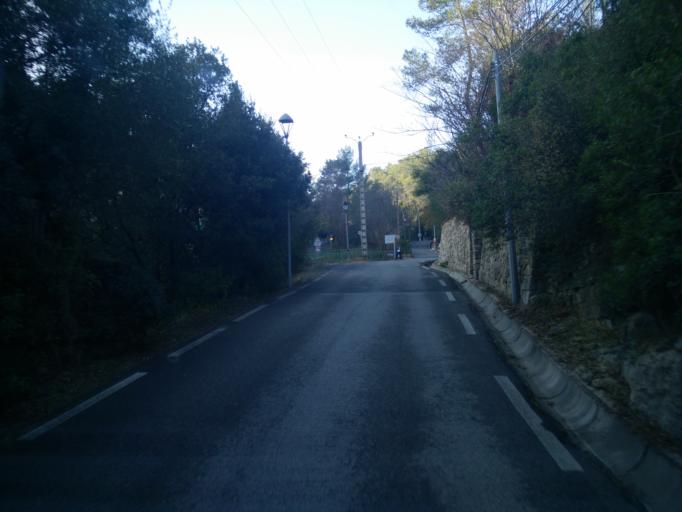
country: FR
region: Provence-Alpes-Cote d'Azur
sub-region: Departement du Var
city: Sollies-Toucas
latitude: 43.2031
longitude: 6.0174
